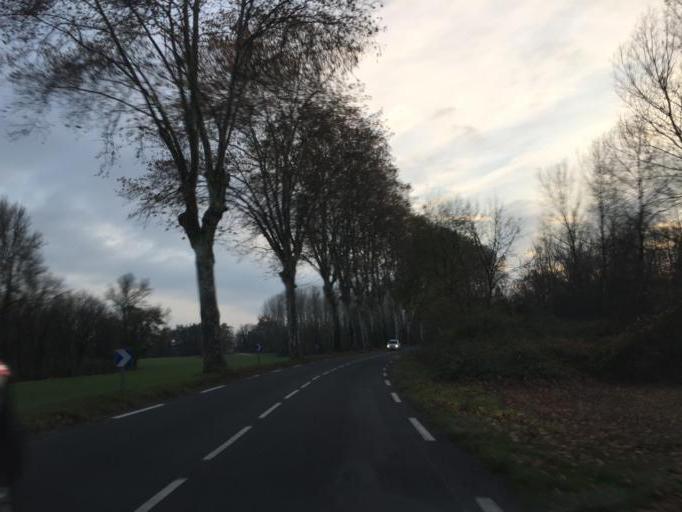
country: FR
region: Rhone-Alpes
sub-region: Departement de l'Ain
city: Chazey-sur-Ain
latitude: 45.9230
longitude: 5.2370
